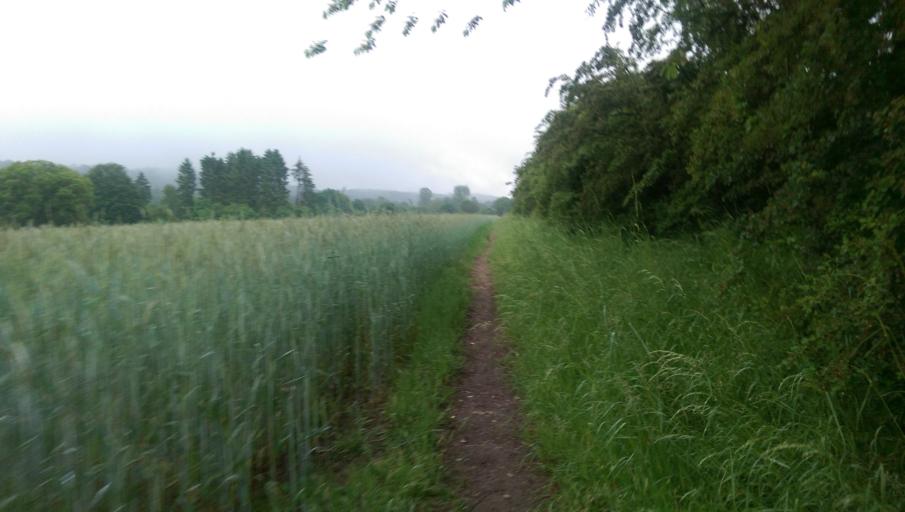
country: DE
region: Saarland
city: Wadgassen
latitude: 49.2510
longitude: 6.7451
